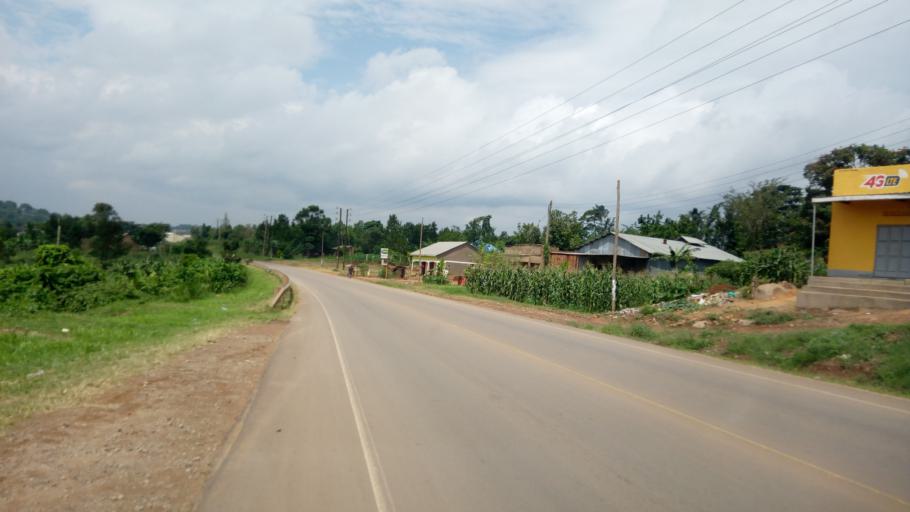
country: UG
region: Central Region
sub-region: Wakiso District
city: Wakiso
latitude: 0.5000
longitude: 32.5226
